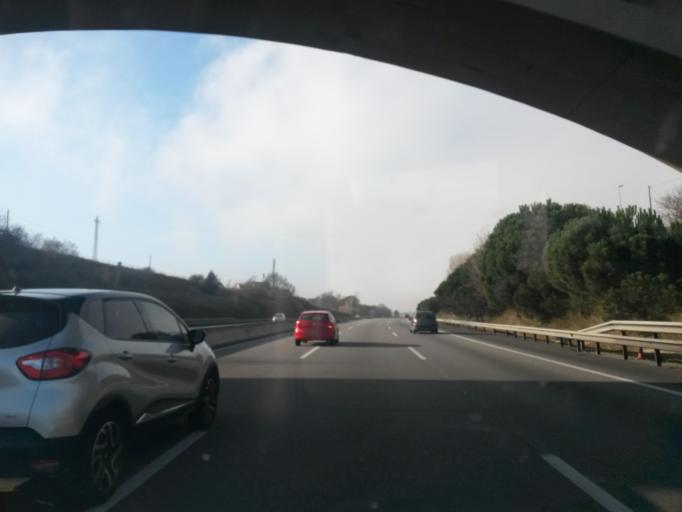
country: ES
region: Catalonia
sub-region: Provincia de Barcelona
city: Llinars del Valles
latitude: 41.6516
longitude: 2.4426
